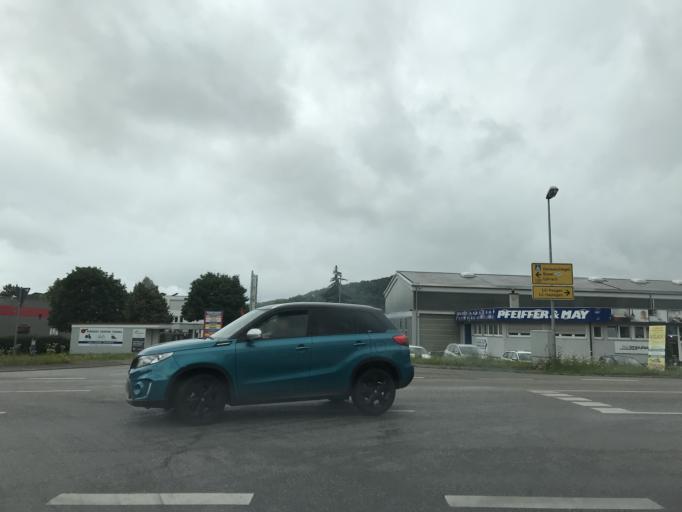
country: DE
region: Baden-Wuerttemberg
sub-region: Freiburg Region
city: Steinen
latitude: 47.6415
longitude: 7.7050
